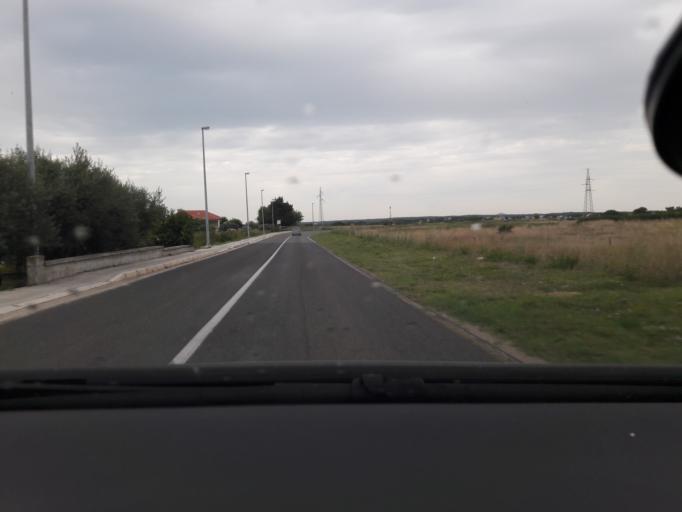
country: HR
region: Zadarska
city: Nin
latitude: 44.2356
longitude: 15.1818
